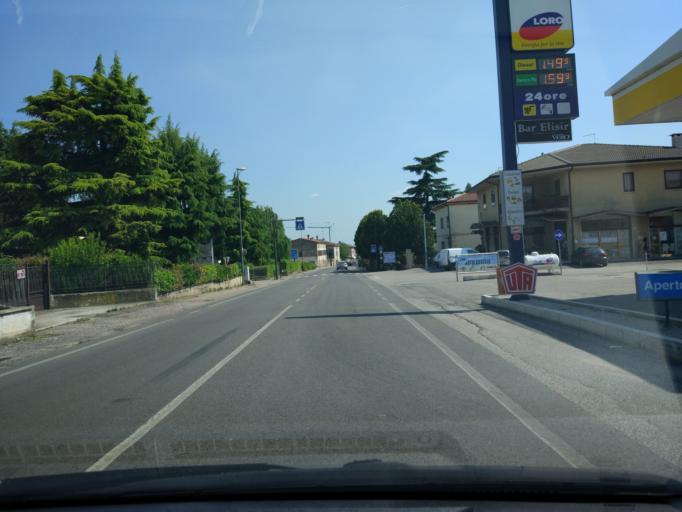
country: IT
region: Veneto
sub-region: Provincia di Verona
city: Cellore
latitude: 45.4881
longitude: 11.1762
